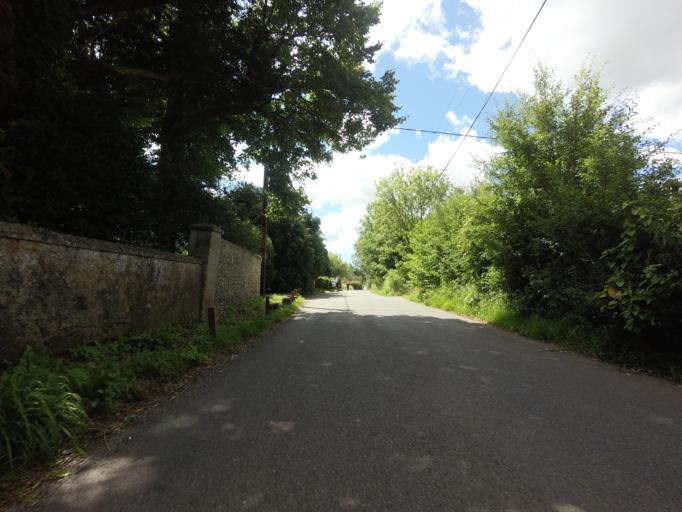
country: GB
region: England
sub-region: East Sussex
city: Ringmer
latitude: 50.8696
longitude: 0.1429
